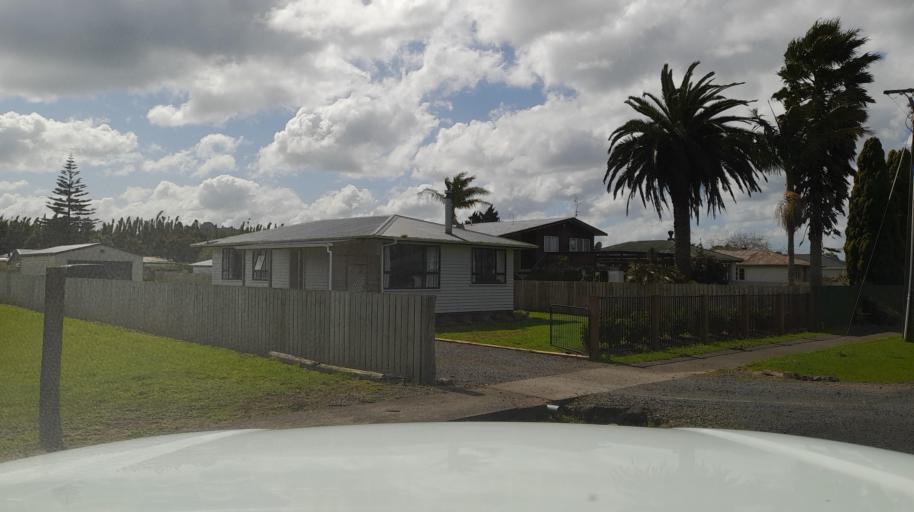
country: NZ
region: Northland
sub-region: Far North District
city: Waimate North
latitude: -35.3537
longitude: 173.8814
